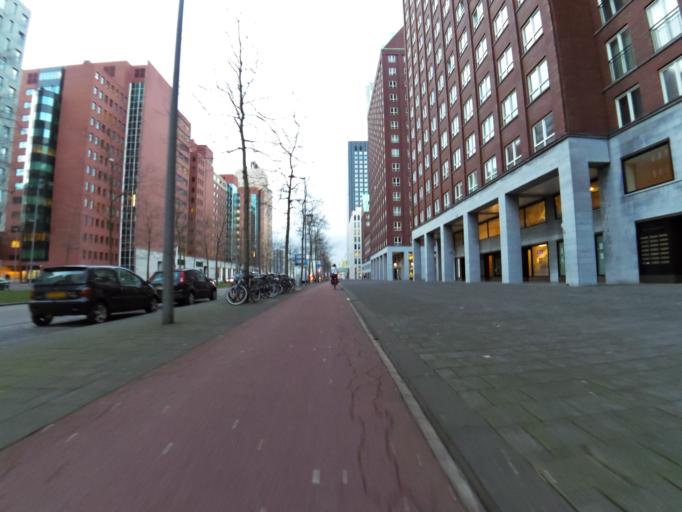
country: NL
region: South Holland
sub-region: Gemeente Rotterdam
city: Rotterdam
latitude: 51.9071
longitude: 4.4963
